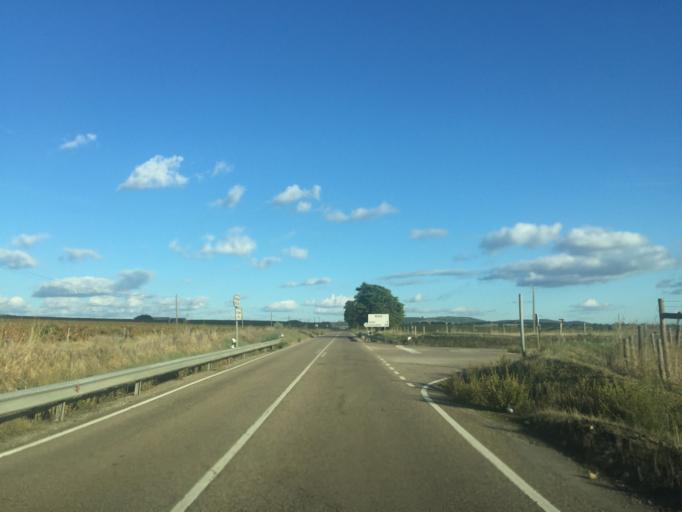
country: PT
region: Portalegre
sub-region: Alter do Chao
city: Alter do Chao
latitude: 39.1960
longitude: -7.6944
